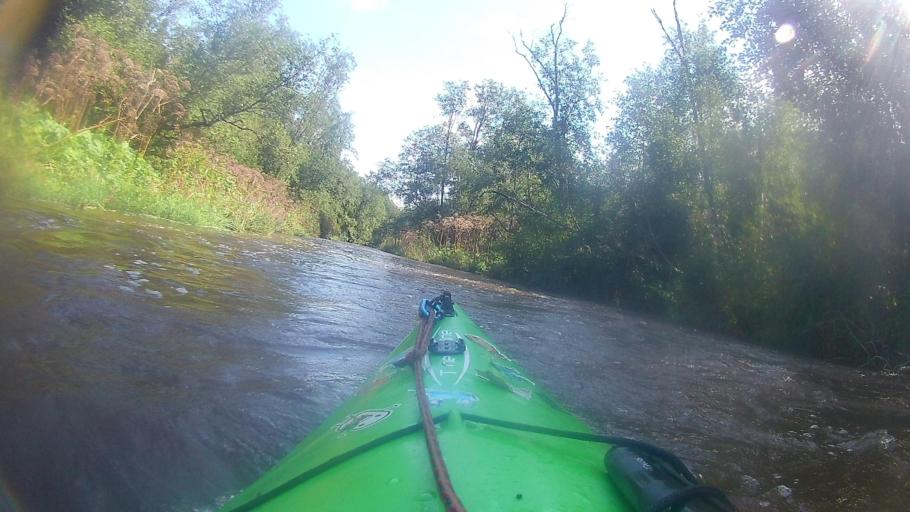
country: LV
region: Talsu Rajons
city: Sabile
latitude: 57.0022
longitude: 22.5978
